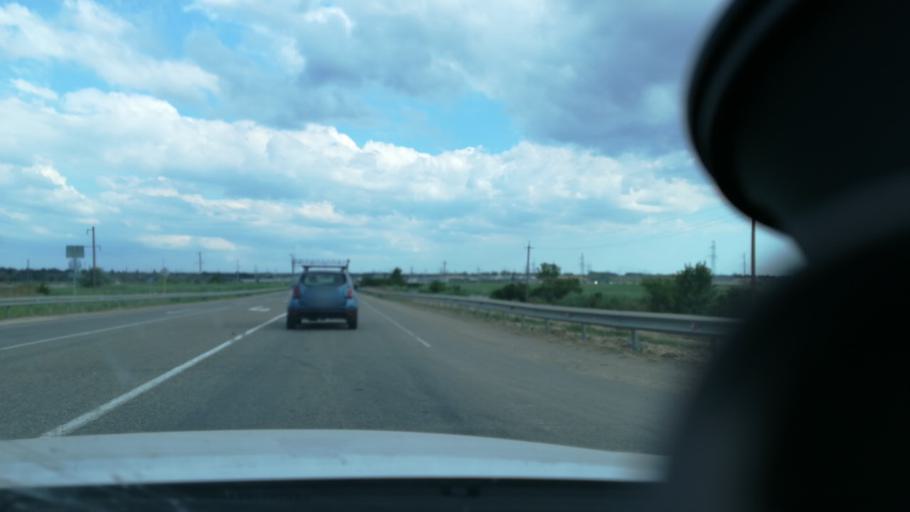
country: RU
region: Krasnodarskiy
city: Dzhiginka
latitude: 45.1465
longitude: 37.3111
